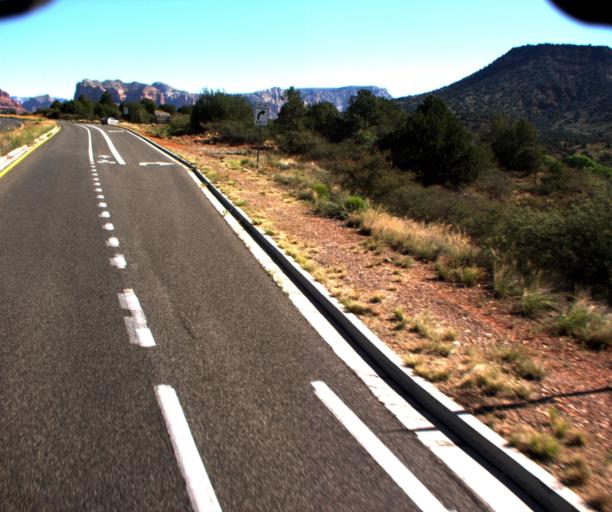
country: US
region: Arizona
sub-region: Yavapai County
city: Big Park
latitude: 34.7548
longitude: -111.7651
